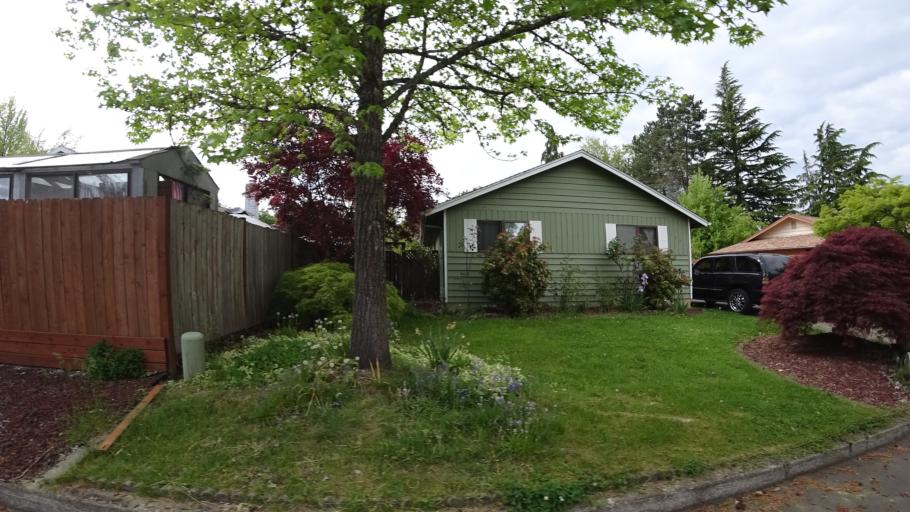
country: US
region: Oregon
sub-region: Washington County
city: Hillsboro
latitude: 45.4999
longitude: -122.9639
